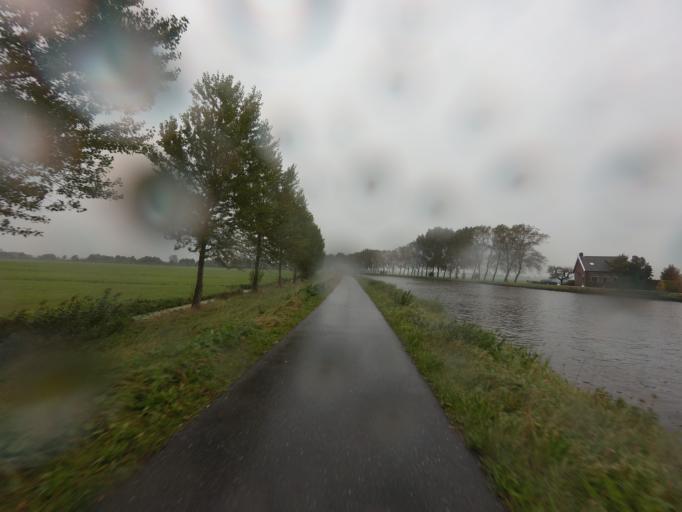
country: NL
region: South Holland
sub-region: Gemeente Leerdam
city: Leerdam
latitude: 51.9296
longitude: 5.0326
